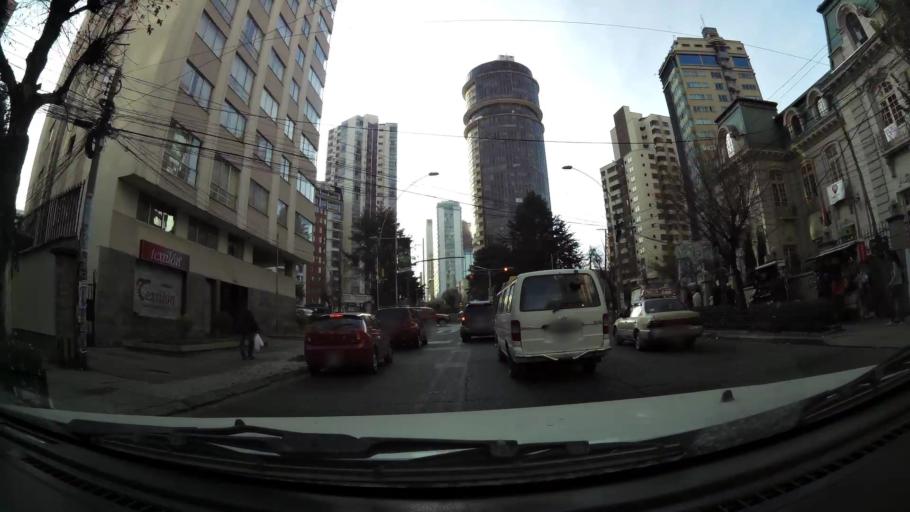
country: BO
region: La Paz
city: La Paz
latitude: -16.5100
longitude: -68.1237
